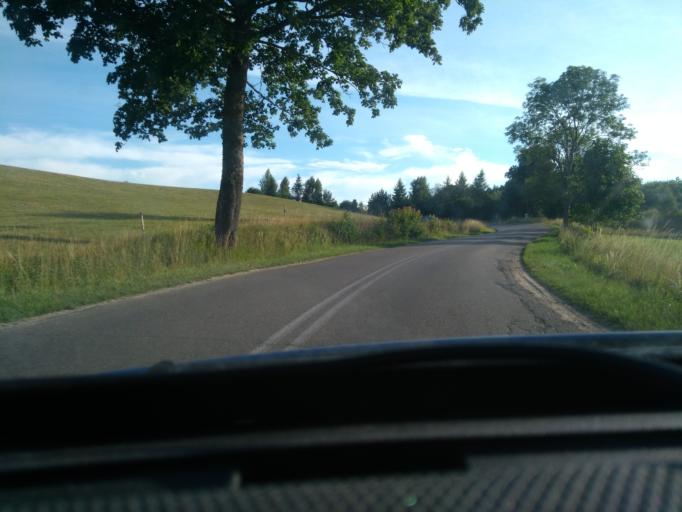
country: PL
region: Pomeranian Voivodeship
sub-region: Powiat kartuski
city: Przodkowo
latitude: 54.3942
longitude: 18.3407
